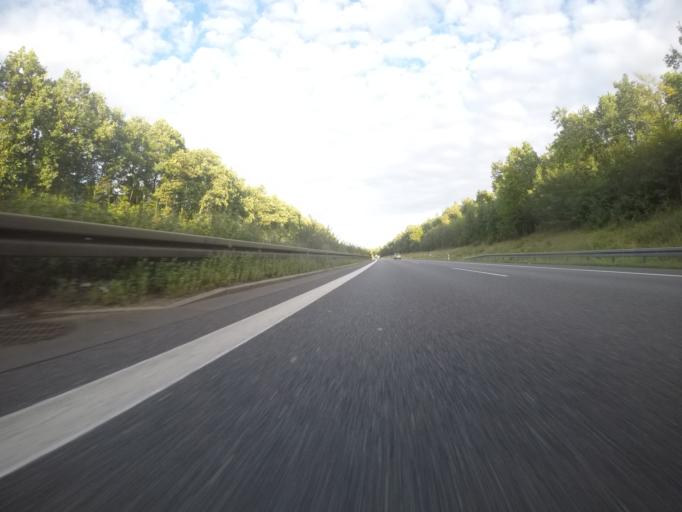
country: DE
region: Bavaria
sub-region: Regierungsbezirk Mittelfranken
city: Rohr
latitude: 49.3056
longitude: 10.9173
